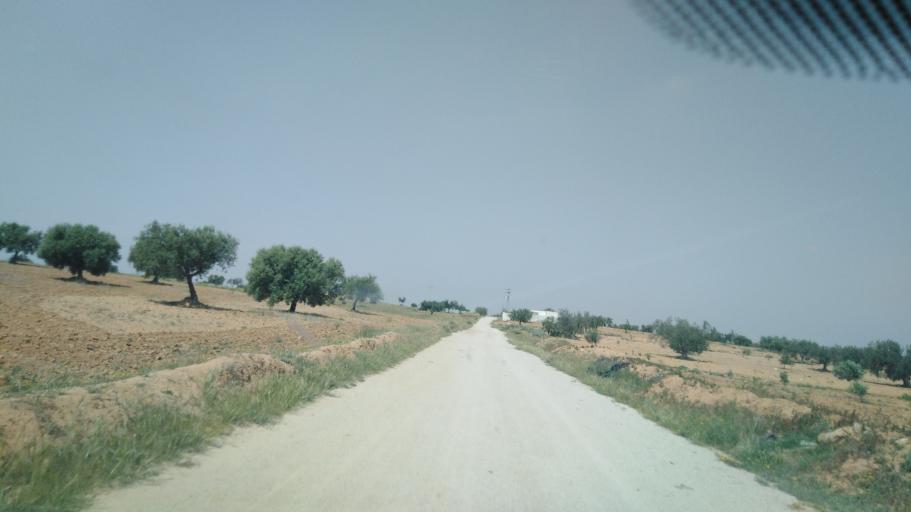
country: TN
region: Safaqis
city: Sfax
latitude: 34.7505
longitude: 10.5657
